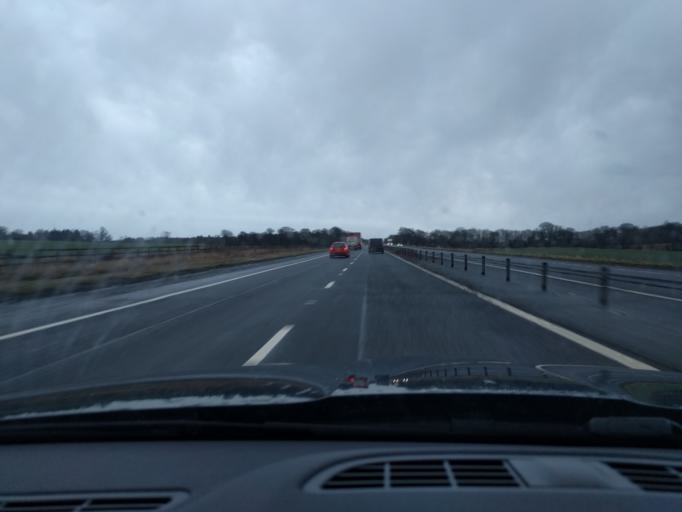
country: GB
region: Scotland
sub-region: West Lothian
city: Broxburn
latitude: 55.9811
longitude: -3.5076
